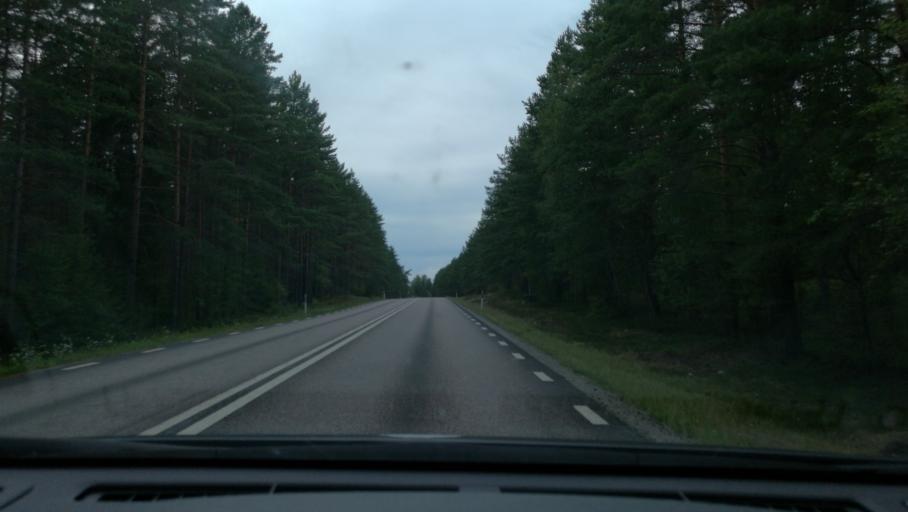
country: SE
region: Soedermanland
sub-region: Katrineholms Kommun
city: Katrineholm
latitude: 59.1300
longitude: 16.1474
